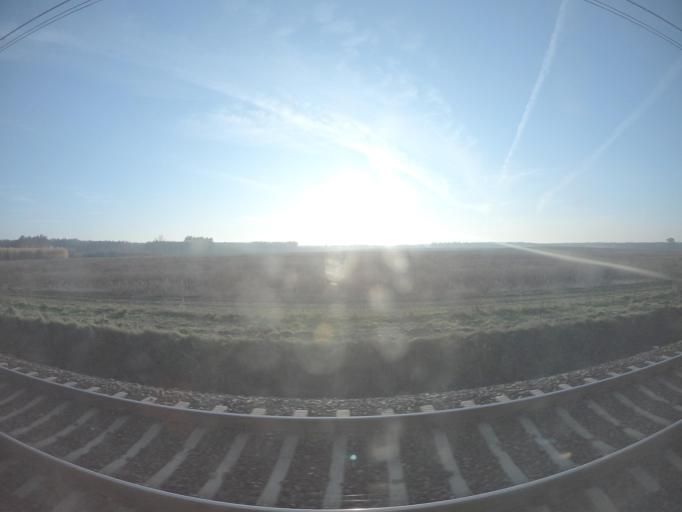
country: PL
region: Lubusz
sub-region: Powiat slubicki
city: Rzepin
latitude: 52.2913
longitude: 14.8874
